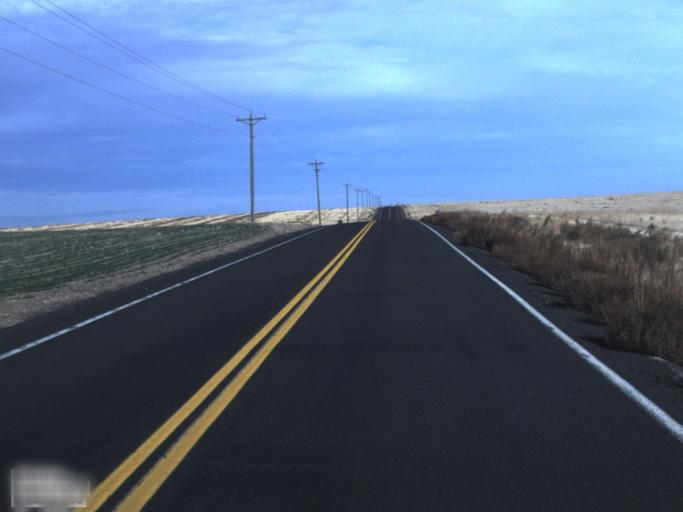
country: US
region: Washington
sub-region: Adams County
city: Ritzville
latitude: 47.2503
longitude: -118.6860
